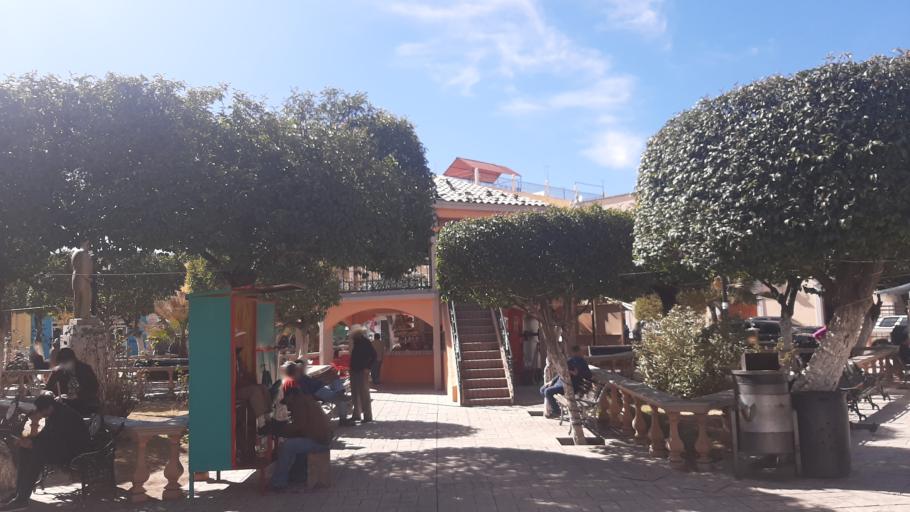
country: MX
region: Durango
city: Santa Catarina de Tepehuanes
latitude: 25.3433
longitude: -105.7236
